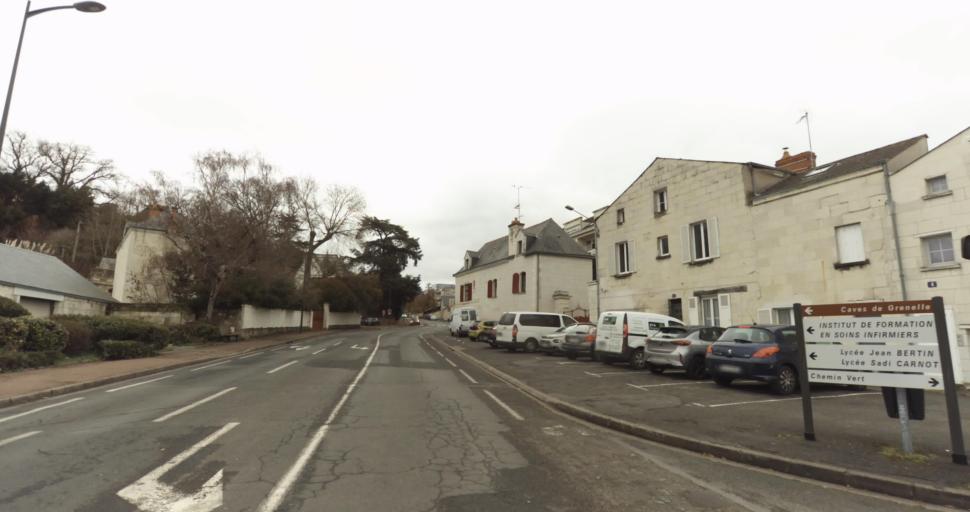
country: FR
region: Pays de la Loire
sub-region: Departement de Maine-et-Loire
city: Saumur
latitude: 47.2515
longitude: -0.0773
